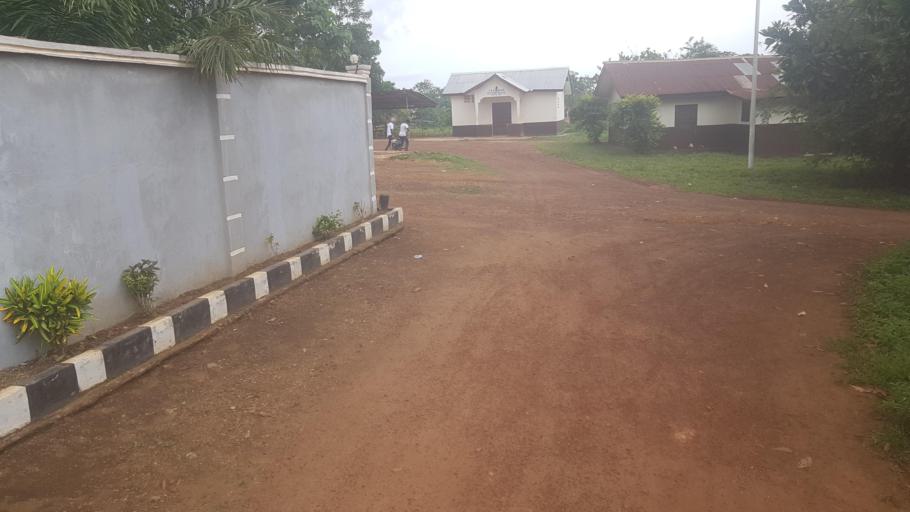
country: SL
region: Southern Province
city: Mogbwemo
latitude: 7.6128
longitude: -12.1757
